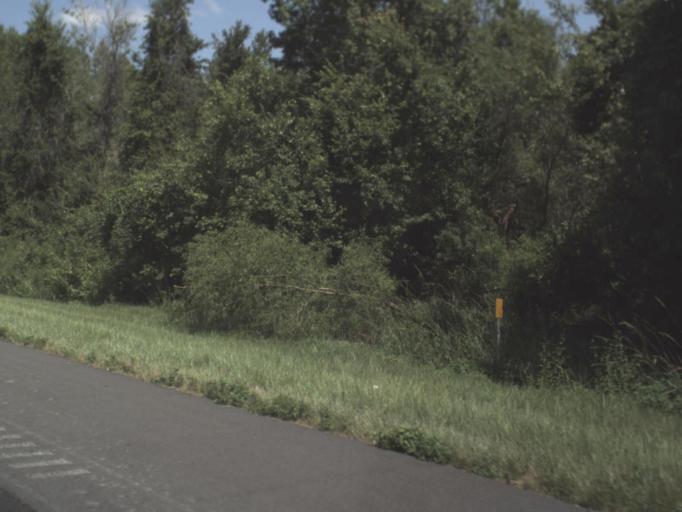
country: US
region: Florida
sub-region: Madison County
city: Madison
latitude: 30.4365
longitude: -83.5116
